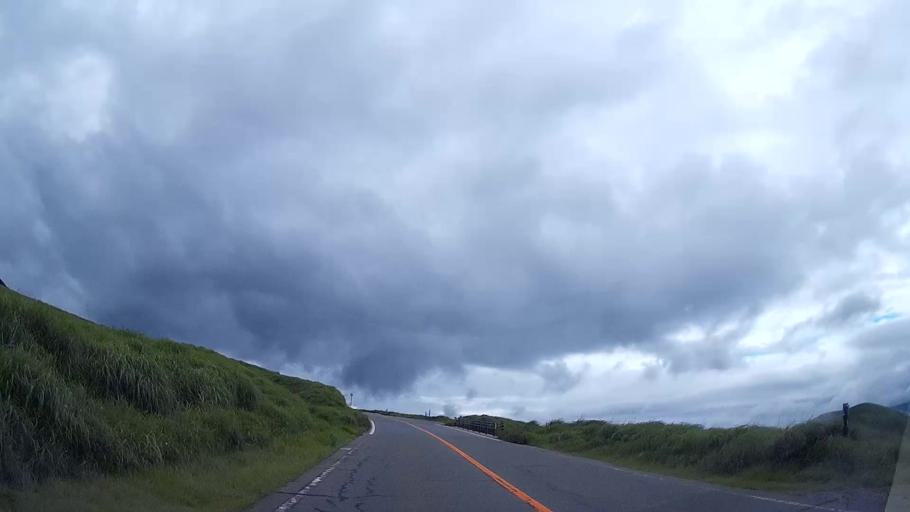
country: JP
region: Kumamoto
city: Aso
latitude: 32.9032
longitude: 131.0533
